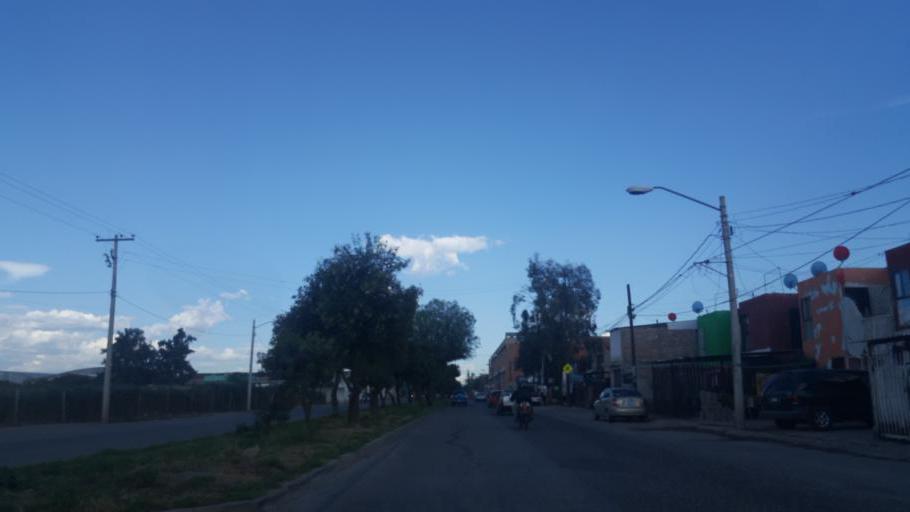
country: MX
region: Guanajuato
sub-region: Leon
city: San Jose de Duran (Los Troncoso)
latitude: 21.0960
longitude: -101.6989
